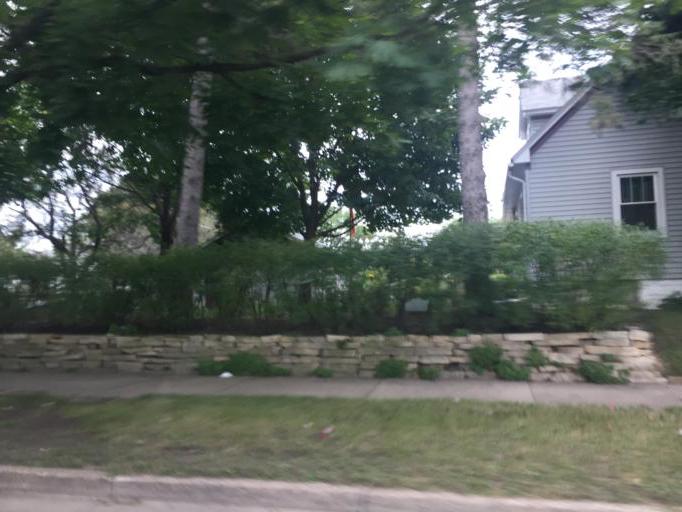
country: US
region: Minnesota
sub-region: Winona County
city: Winona
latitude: 44.0489
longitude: -91.6613
